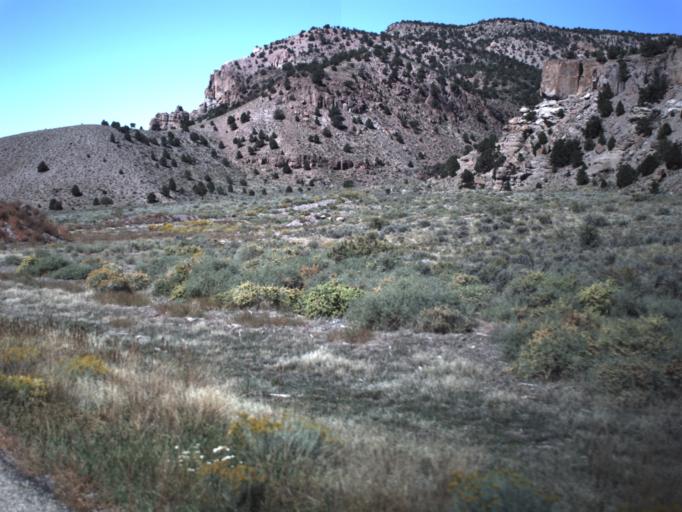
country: US
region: Utah
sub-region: Piute County
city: Junction
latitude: 38.1888
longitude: -112.0959
